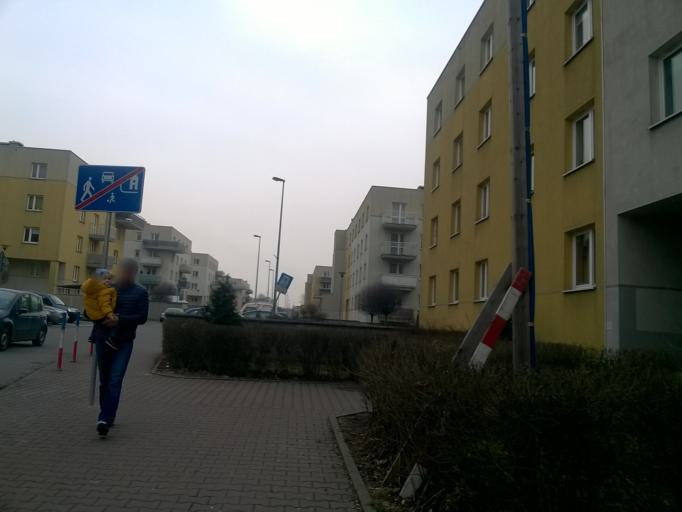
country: PL
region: Lesser Poland Voivodeship
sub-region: Krakow
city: Krakow
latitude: 50.0846
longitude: 19.9813
